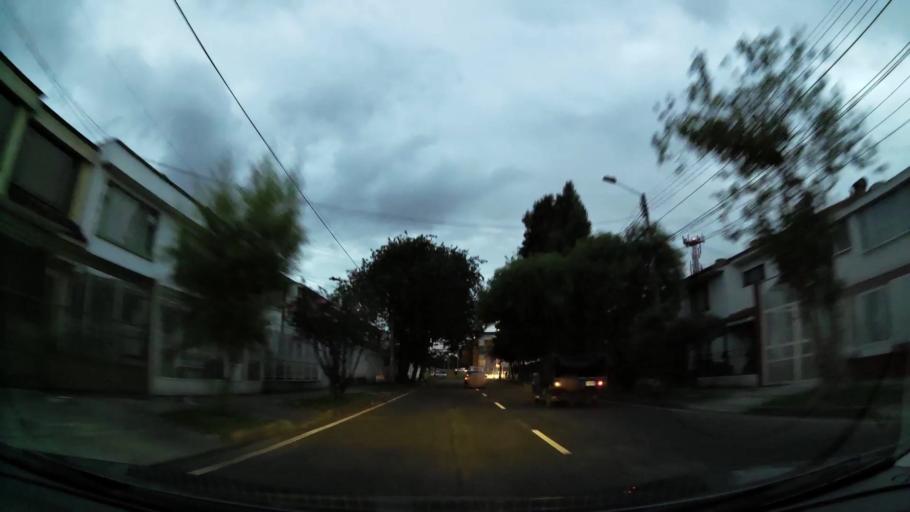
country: CO
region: Bogota D.C.
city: Bogota
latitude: 4.6688
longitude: -74.1110
